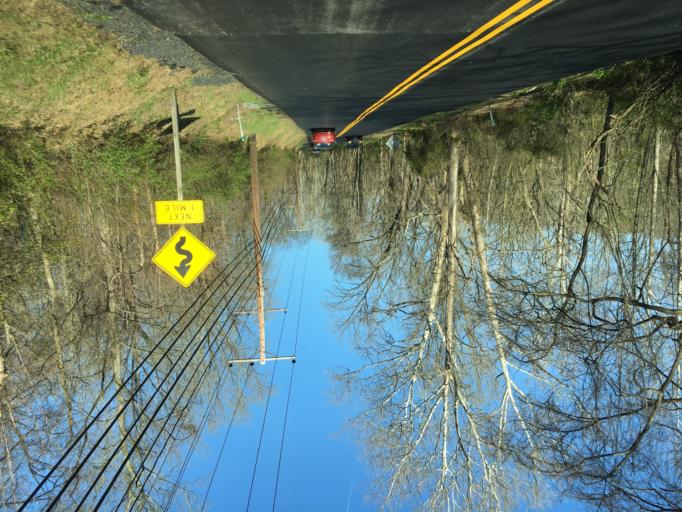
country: US
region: Maryland
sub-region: Baltimore County
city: Hunt Valley
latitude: 39.5065
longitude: -76.6117
